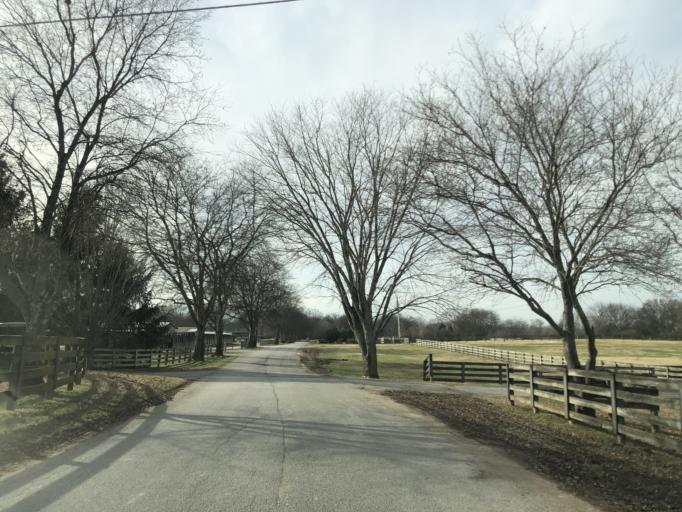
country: US
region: Tennessee
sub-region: Williamson County
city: Franklin
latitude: 35.9483
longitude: -86.8849
